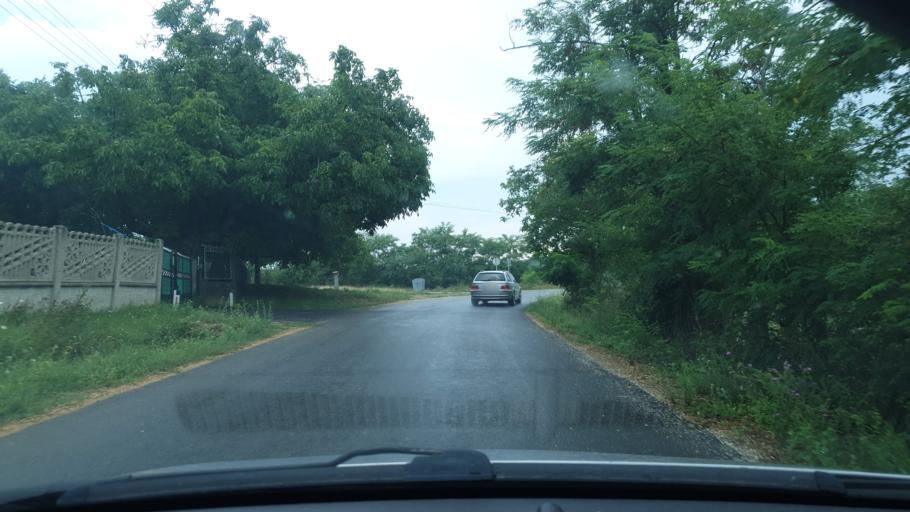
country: RS
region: Central Serbia
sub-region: Sumadijski Okrug
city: Kragujevac
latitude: 44.0647
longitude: 20.7909
